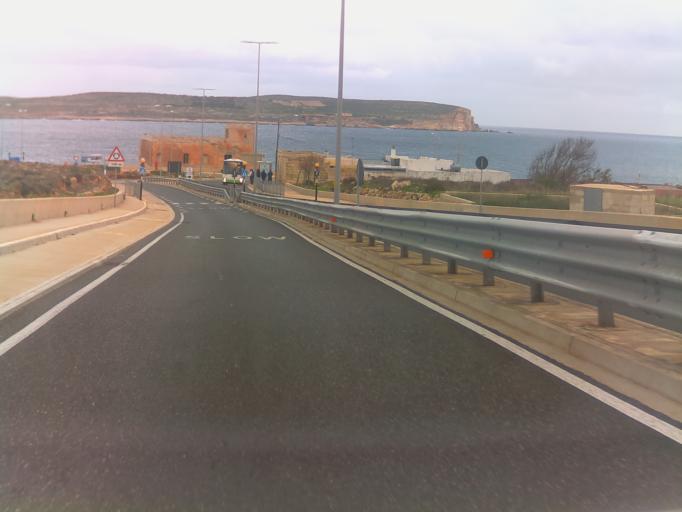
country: MT
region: Il-Mellieha
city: Mellieha
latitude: 35.9847
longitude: 14.3420
